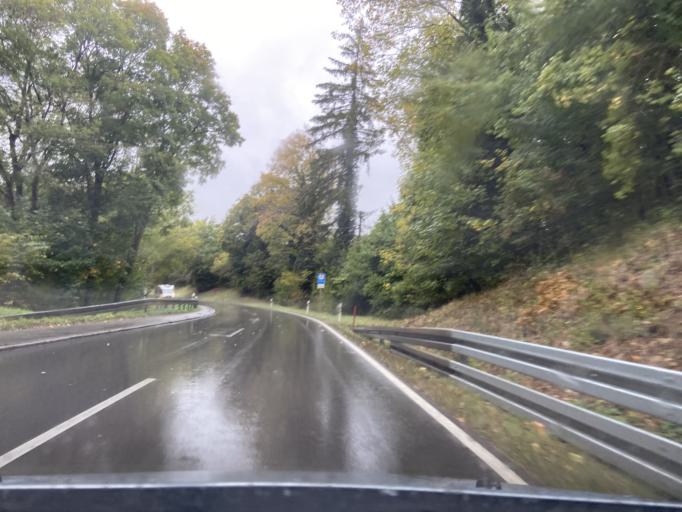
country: DE
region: Baden-Wuerttemberg
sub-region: Tuebingen Region
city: Scheer
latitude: 48.0772
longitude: 9.2943
